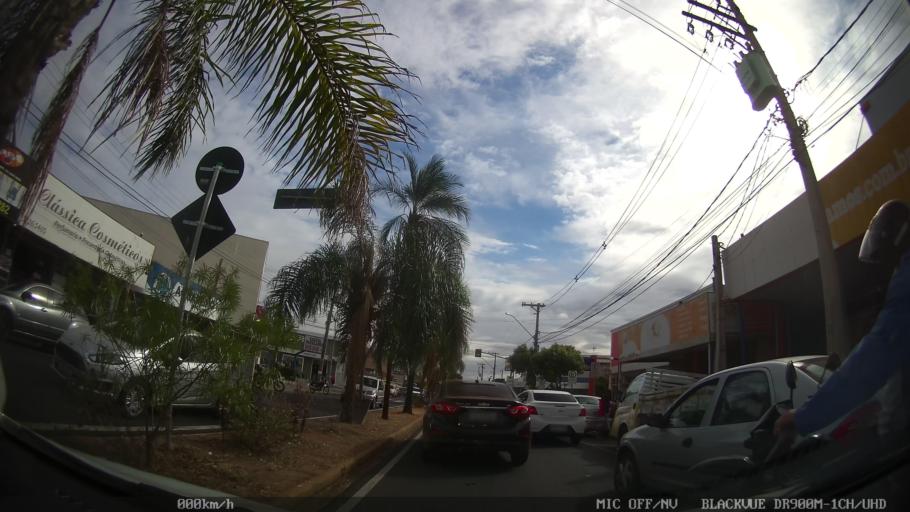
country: BR
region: Sao Paulo
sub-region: Sao Jose Do Rio Preto
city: Sao Jose do Rio Preto
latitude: -20.8287
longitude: -49.3729
